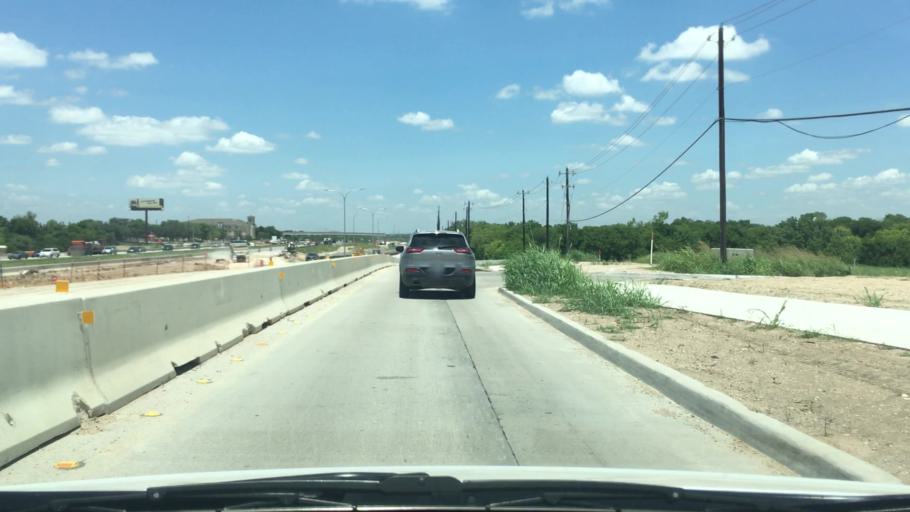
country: US
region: Texas
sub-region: Travis County
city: Austin
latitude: 30.2871
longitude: -97.6644
